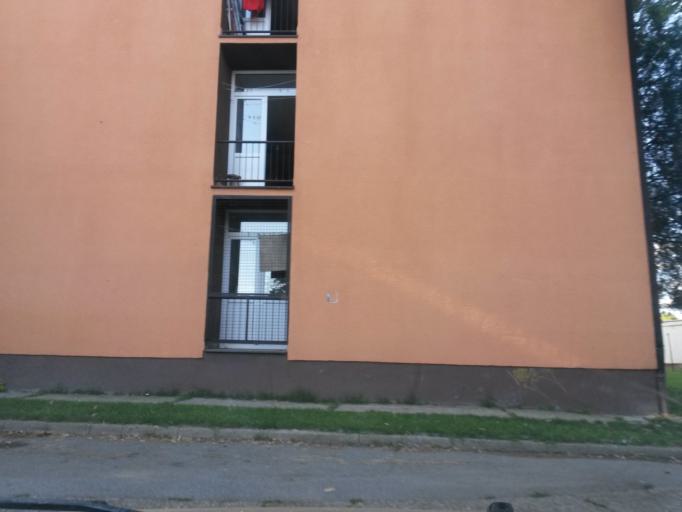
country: HR
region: Osjecko-Baranjska
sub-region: Grad Osijek
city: Osijek
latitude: 45.5528
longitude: 18.7053
